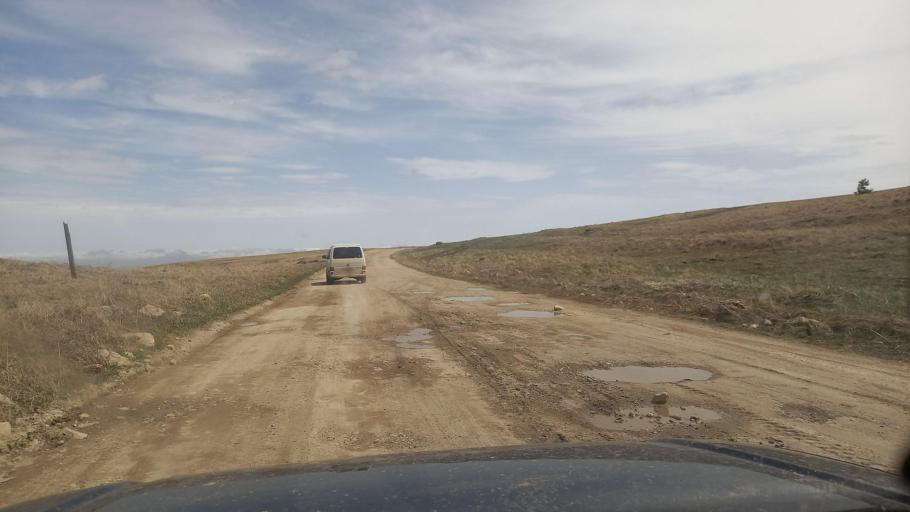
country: RU
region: Stavropol'skiy
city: Kislovodsk
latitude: 43.7509
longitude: 42.7096
